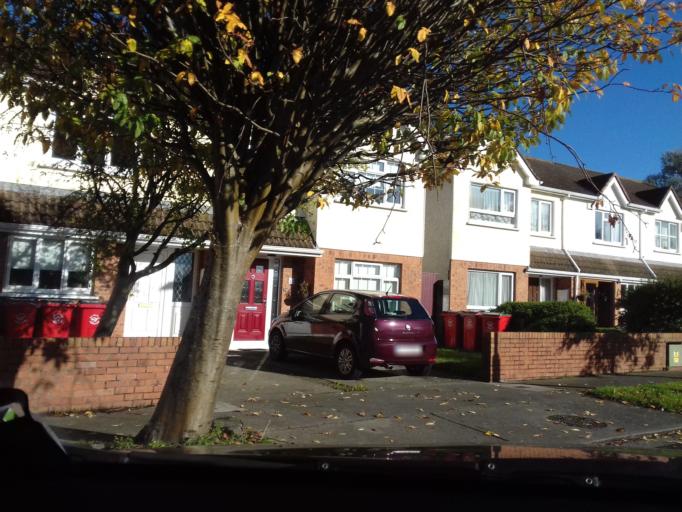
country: IE
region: Leinster
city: Cabra
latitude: 53.3624
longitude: -6.3047
